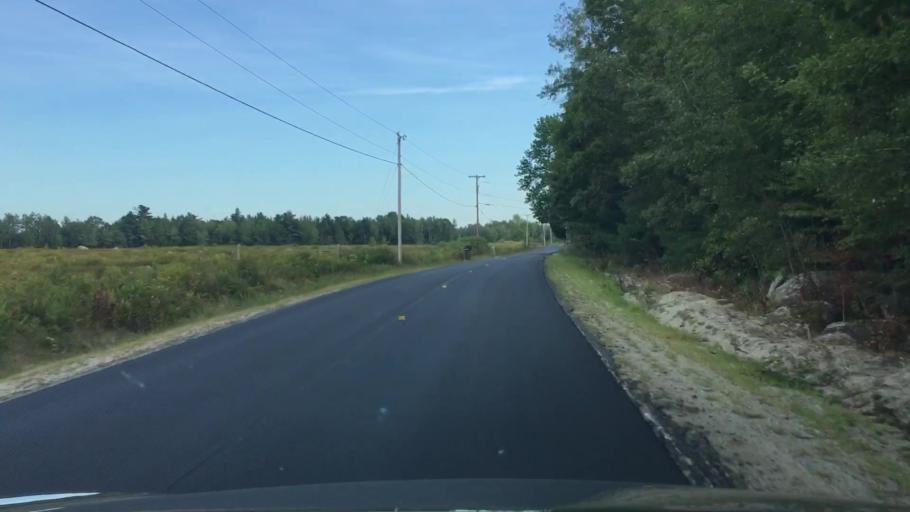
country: US
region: Maine
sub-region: Hancock County
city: Surry
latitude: 44.5361
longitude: -68.6145
